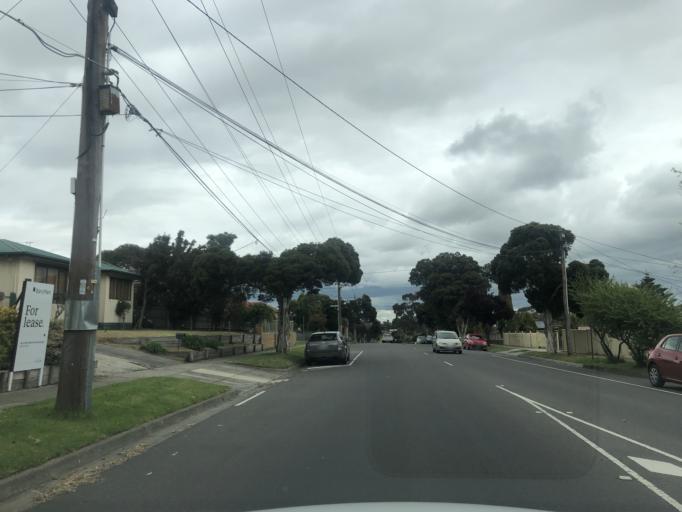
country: AU
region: Victoria
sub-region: Greater Dandenong
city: Noble Park North
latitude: -37.9549
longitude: 145.1922
